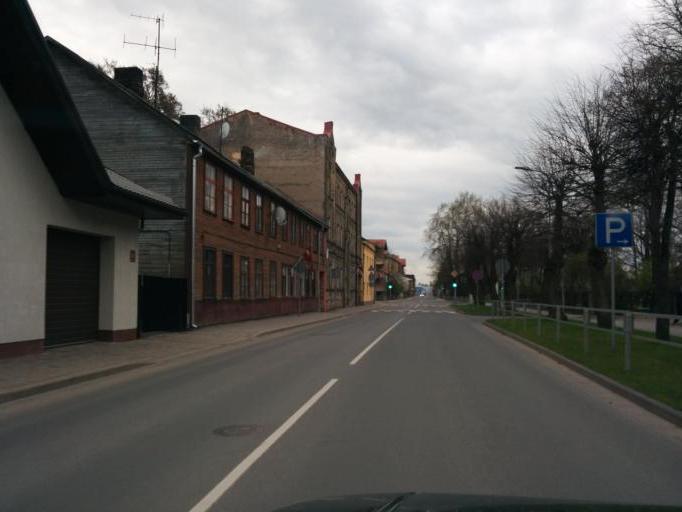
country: LV
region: Jelgava
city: Jelgava
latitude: 56.6441
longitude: 23.7232
